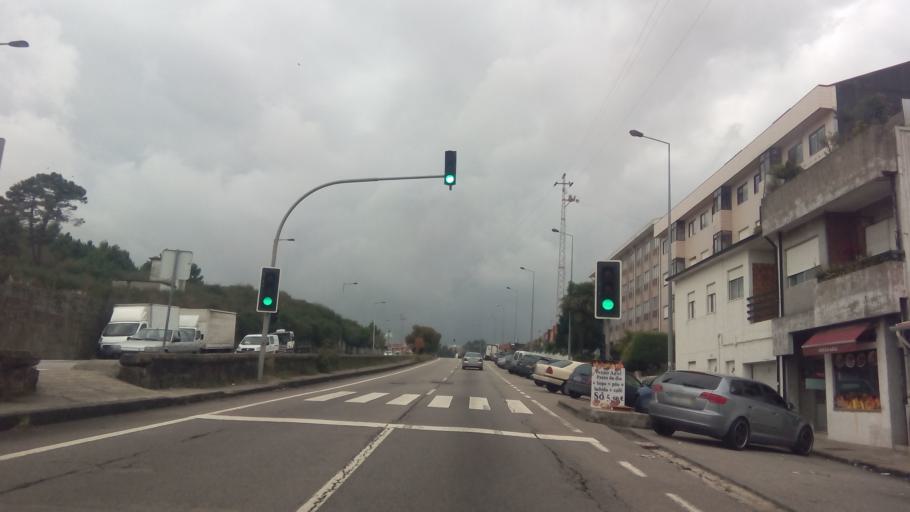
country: PT
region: Porto
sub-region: Gondomar
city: Rio Tinto
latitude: 41.1770
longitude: -8.5672
